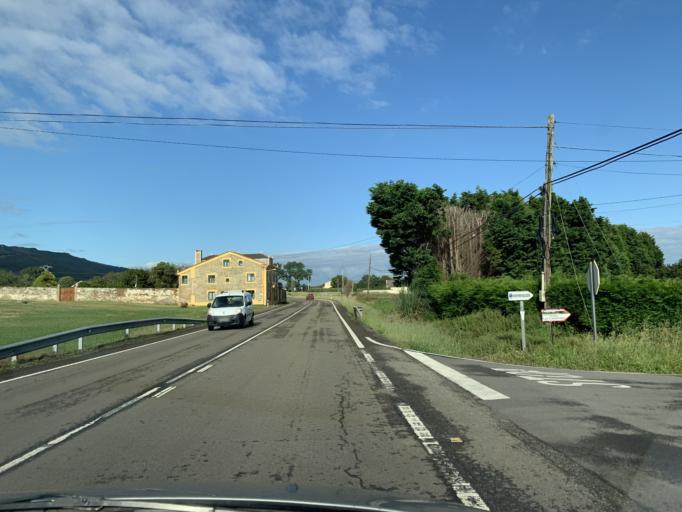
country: ES
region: Galicia
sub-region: Provincia de Lugo
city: Ribadeo
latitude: 43.5470
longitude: -7.1161
